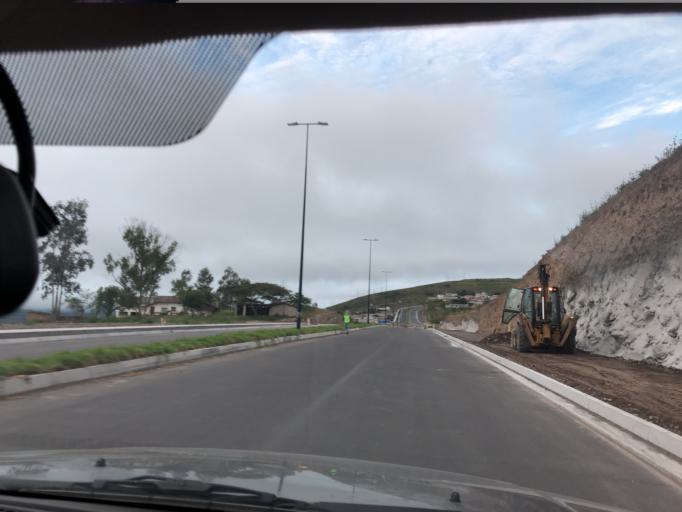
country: EC
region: Imbabura
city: Ibarra
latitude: 0.3607
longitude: -78.1396
